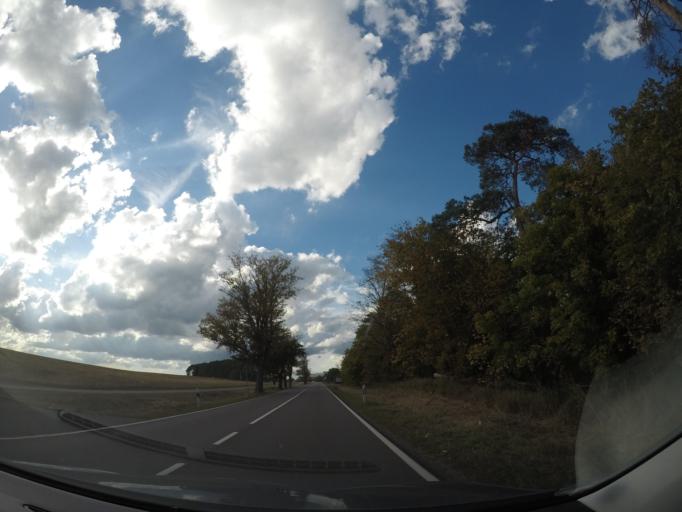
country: DE
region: Saxony-Anhalt
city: Bulstringen
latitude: 52.3056
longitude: 11.3629
